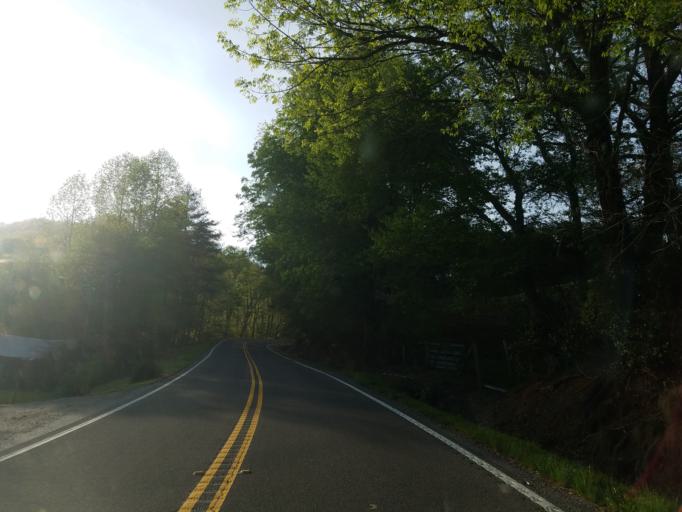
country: US
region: Georgia
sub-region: Fannin County
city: Blue Ridge
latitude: 34.7580
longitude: -84.1476
